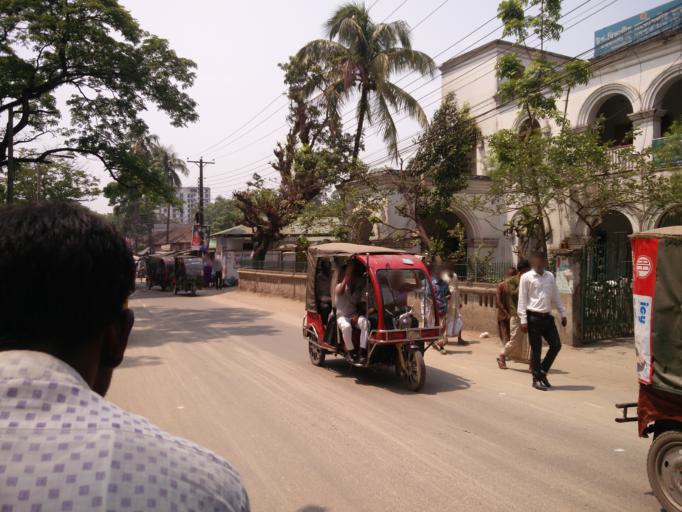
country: BD
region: Dhaka
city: Mymensingh
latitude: 24.7636
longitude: 90.4059
